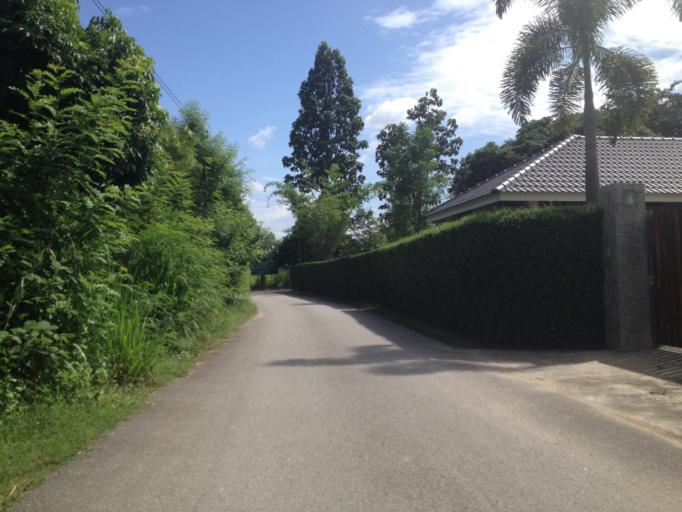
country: TH
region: Chiang Mai
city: Hang Dong
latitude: 18.6814
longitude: 98.8790
